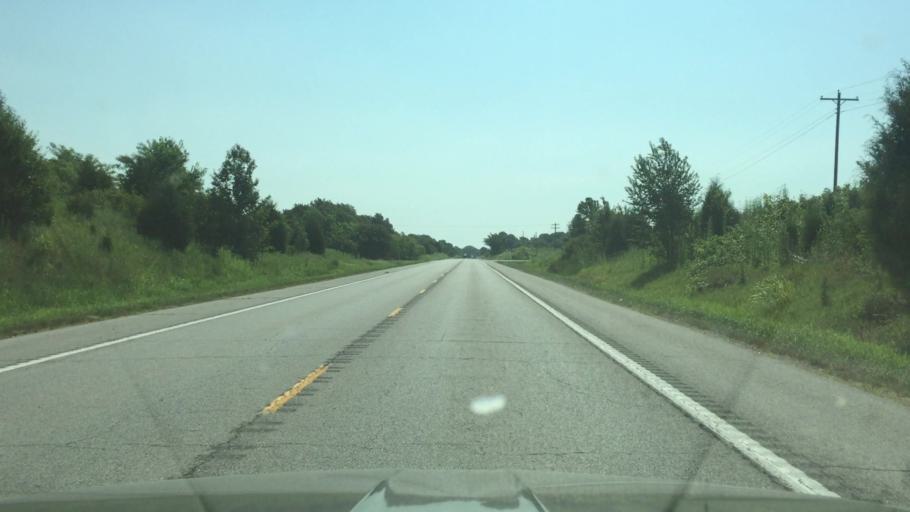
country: US
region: Missouri
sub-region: Pettis County
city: Sedalia
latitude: 38.6935
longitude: -93.0892
